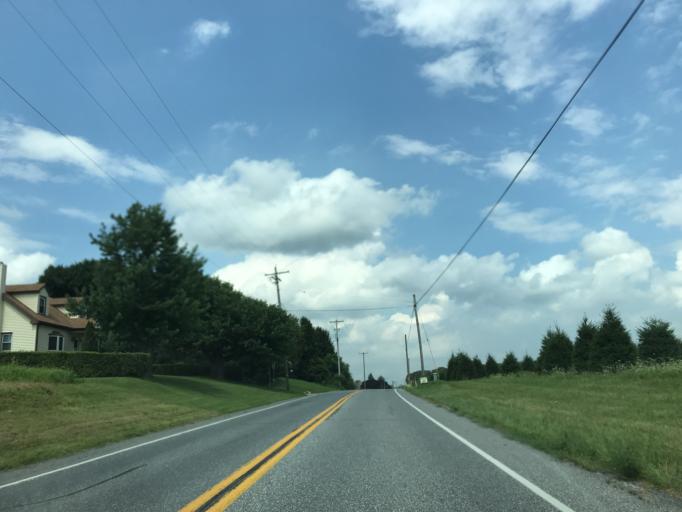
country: US
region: Pennsylvania
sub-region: York County
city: Red Lion
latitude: 39.8581
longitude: -76.6211
